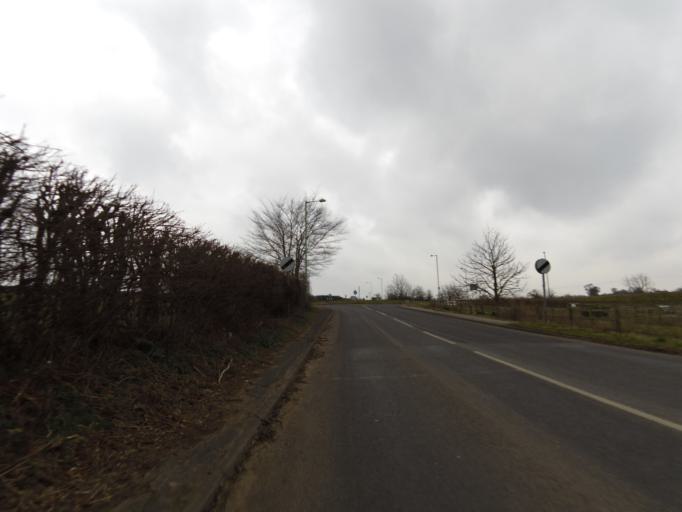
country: GB
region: England
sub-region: Suffolk
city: Wickham Market
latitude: 52.1610
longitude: 1.3782
